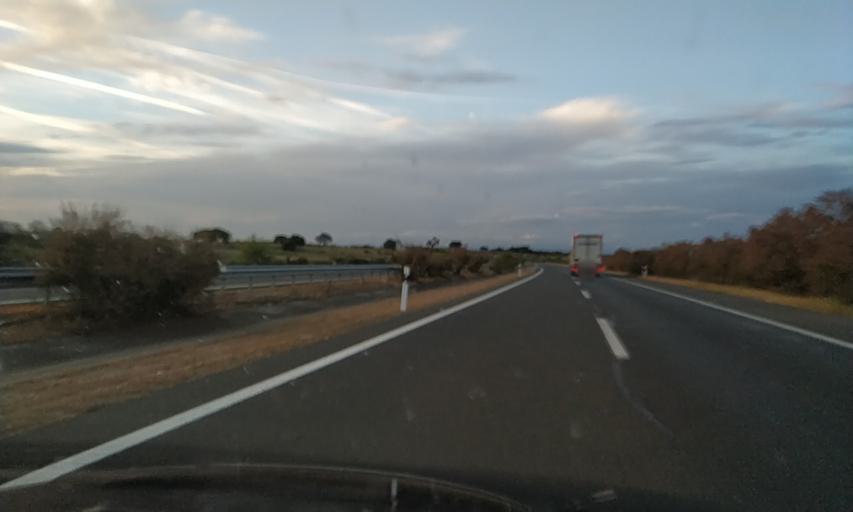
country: ES
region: Extremadura
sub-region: Provincia de Caceres
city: Aldea del Cano
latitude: 39.3077
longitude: -6.3276
